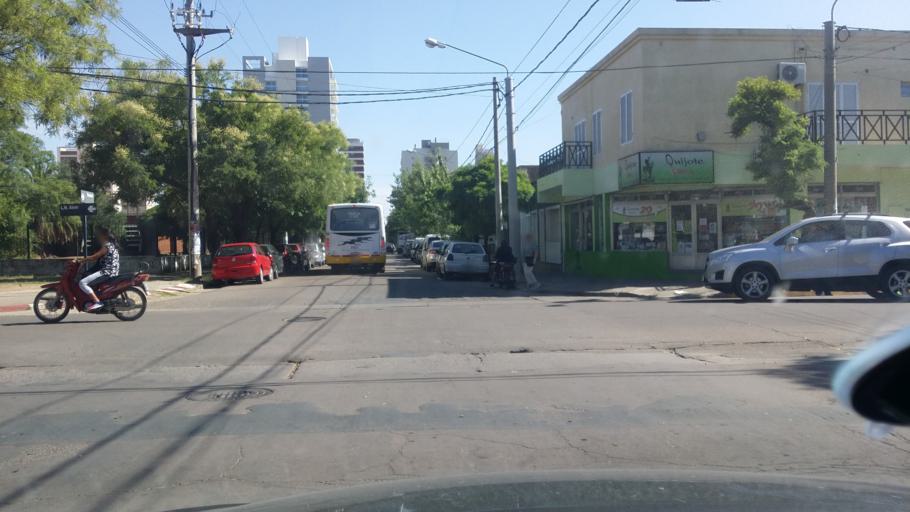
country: AR
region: La Pampa
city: Santa Rosa
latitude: -36.6232
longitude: -64.2873
